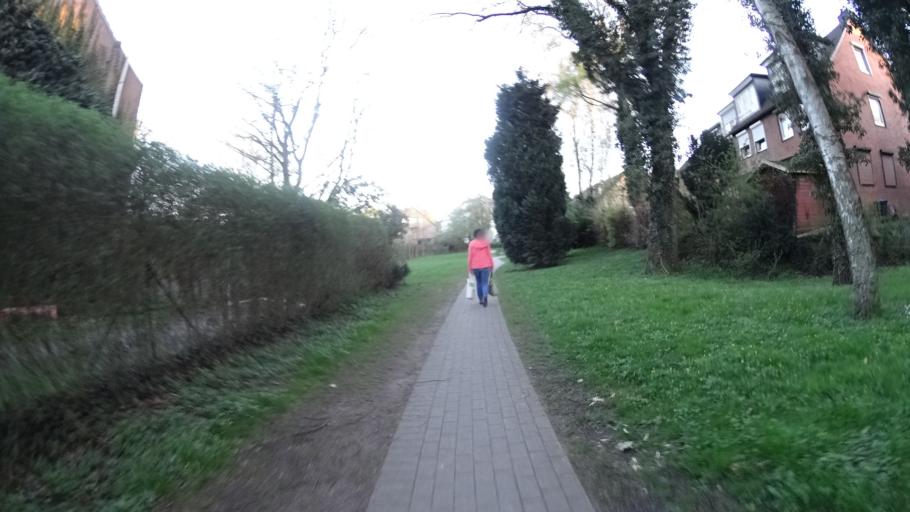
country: DE
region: Hamburg
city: Stellingen
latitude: 53.6285
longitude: 9.9517
